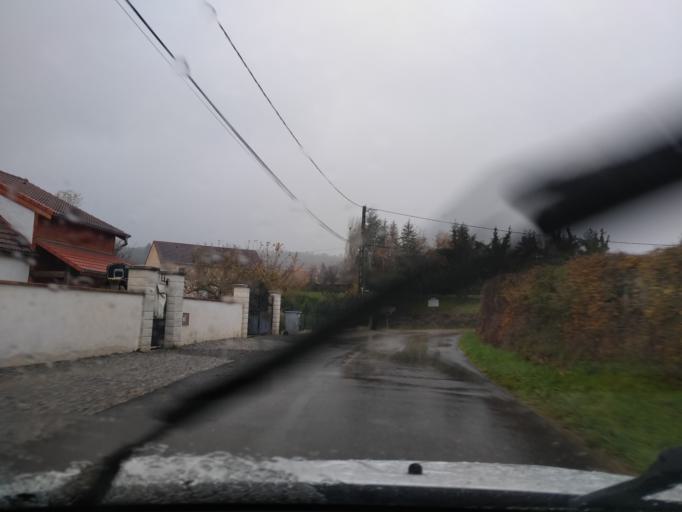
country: FR
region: Bourgogne
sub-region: Departement de Saone-et-Loire
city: Saint-Leger-sur-Dheune
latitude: 46.8859
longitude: 4.6483
